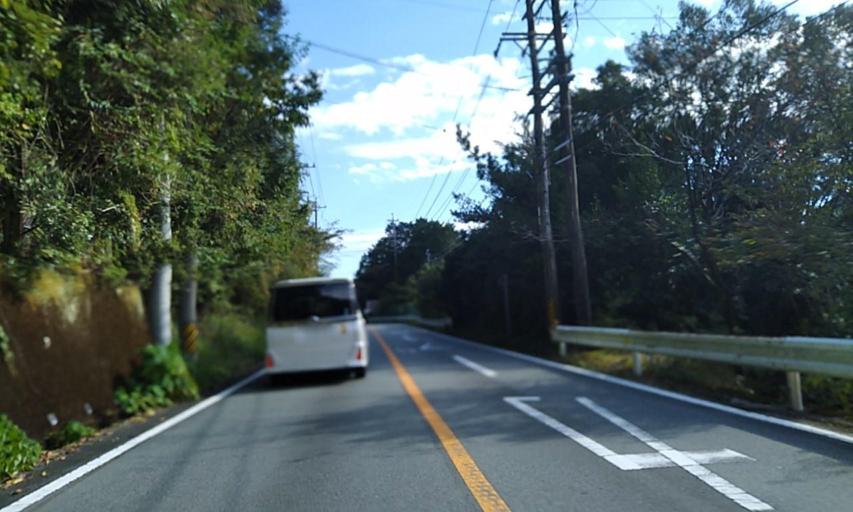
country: JP
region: Mie
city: Owase
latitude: 34.2183
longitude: 136.3844
